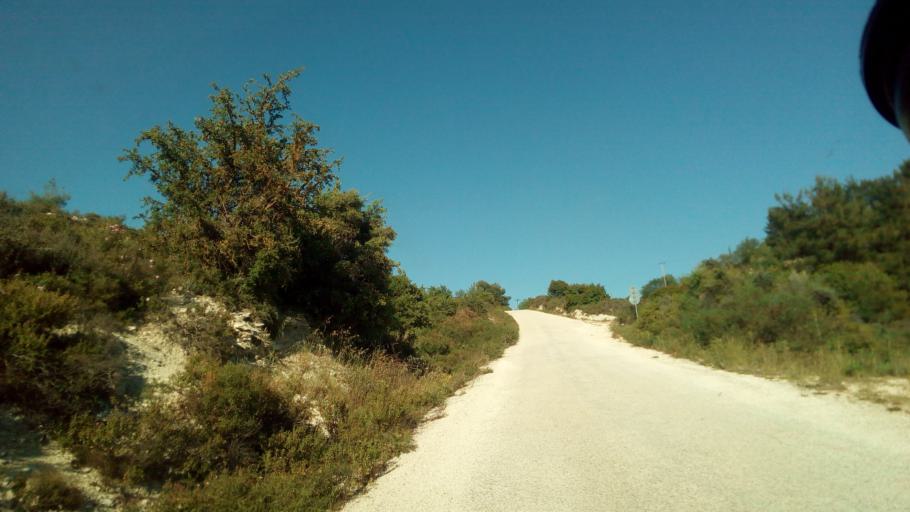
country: CY
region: Limassol
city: Pachna
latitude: 34.8679
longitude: 32.7578
